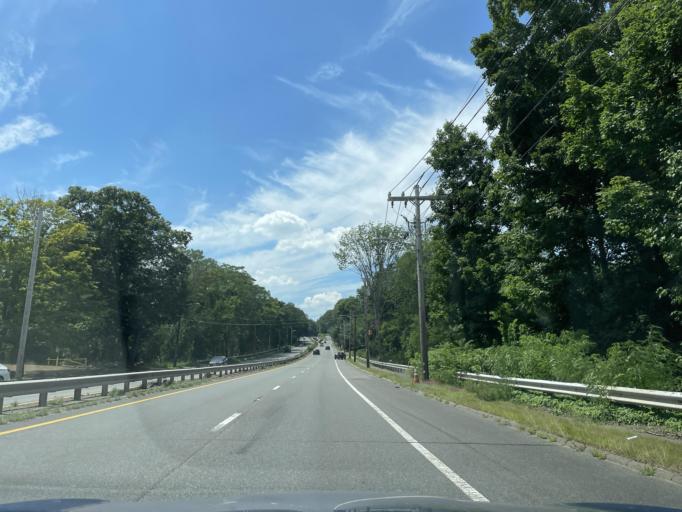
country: US
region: Massachusetts
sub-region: Norfolk County
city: Needham
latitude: 42.3148
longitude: -71.2535
